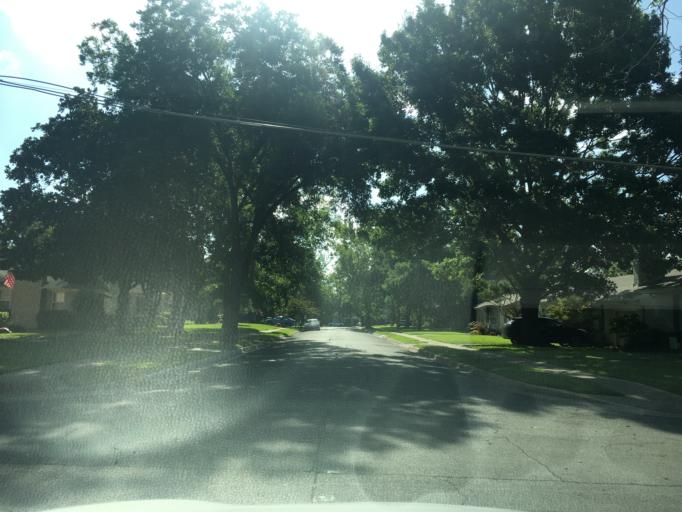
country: US
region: Texas
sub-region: Dallas County
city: Highland Park
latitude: 32.8342
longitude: -96.7468
